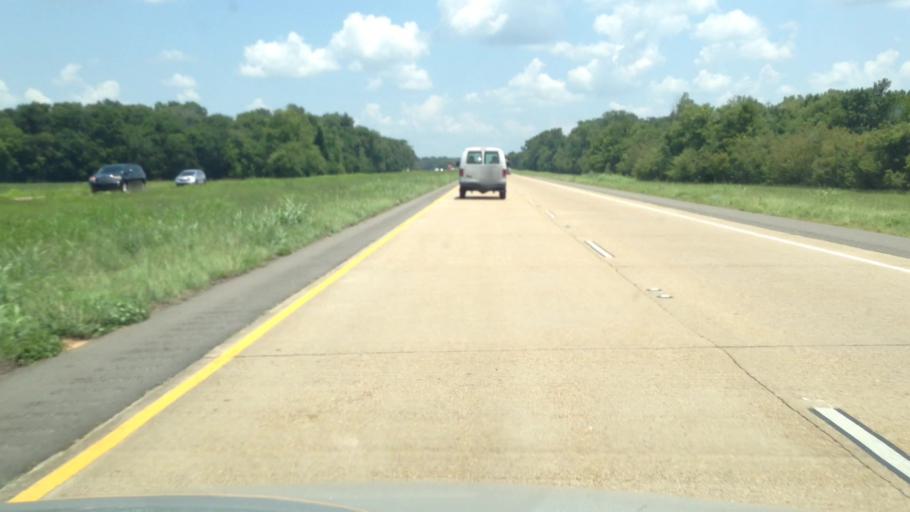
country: US
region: Louisiana
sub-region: Rapides Parish
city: Lecompte
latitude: 31.0082
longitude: -92.3602
